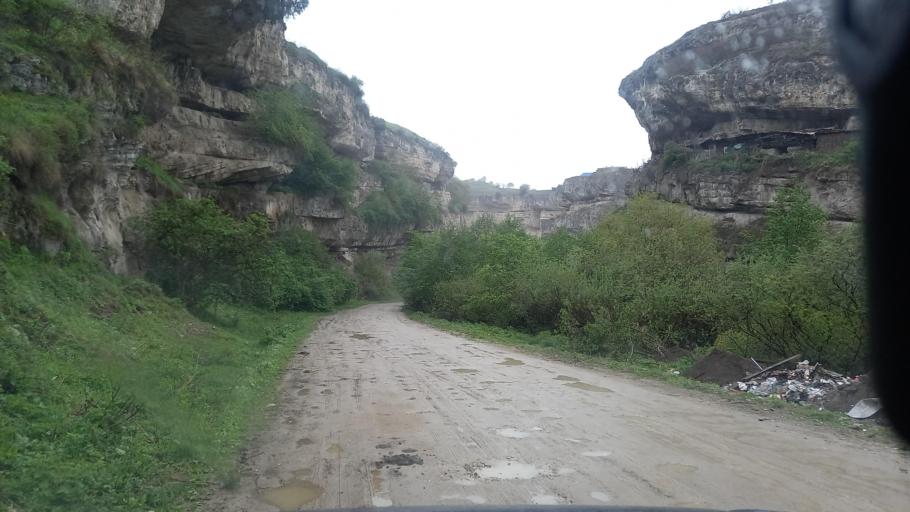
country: RU
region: Kabardino-Balkariya
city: Gundelen
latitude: 43.5972
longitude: 43.1485
